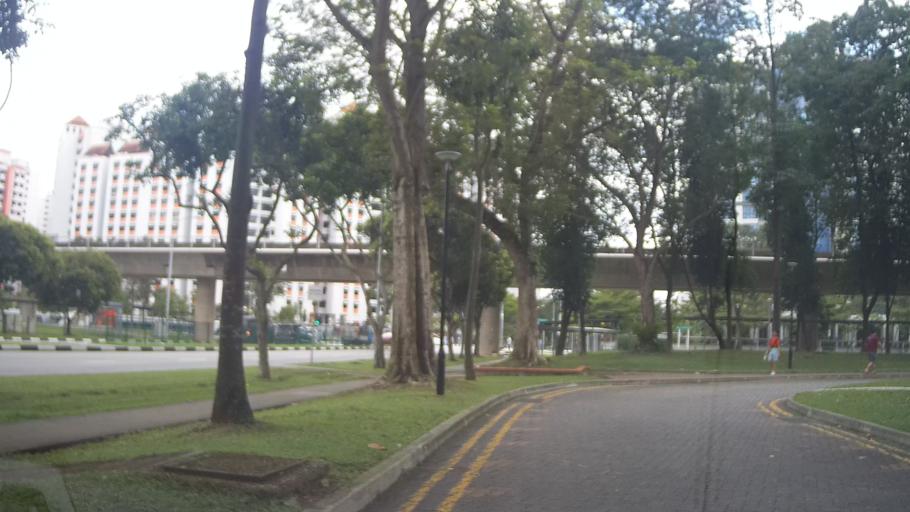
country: MY
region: Johor
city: Johor Bahru
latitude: 1.4005
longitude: 103.7476
